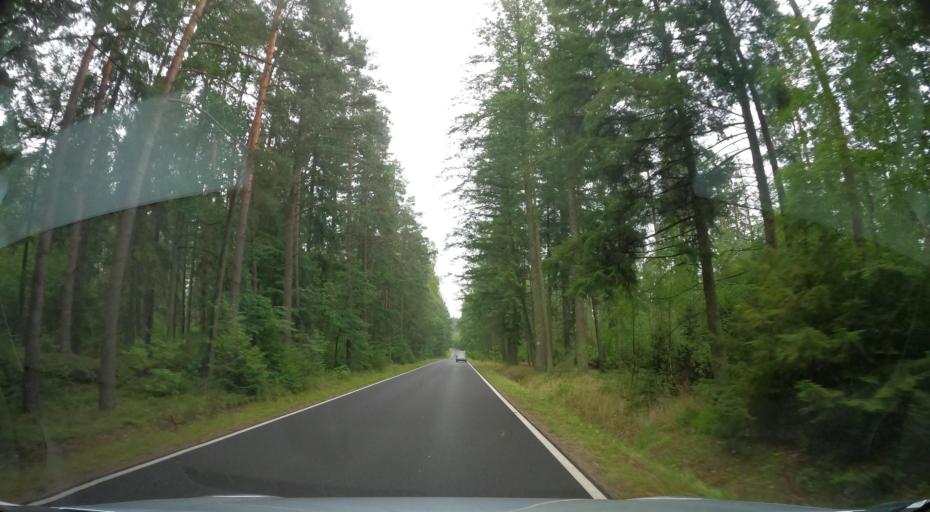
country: PL
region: Pomeranian Voivodeship
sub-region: Powiat wejherowski
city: Linia
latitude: 54.4887
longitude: 17.8432
